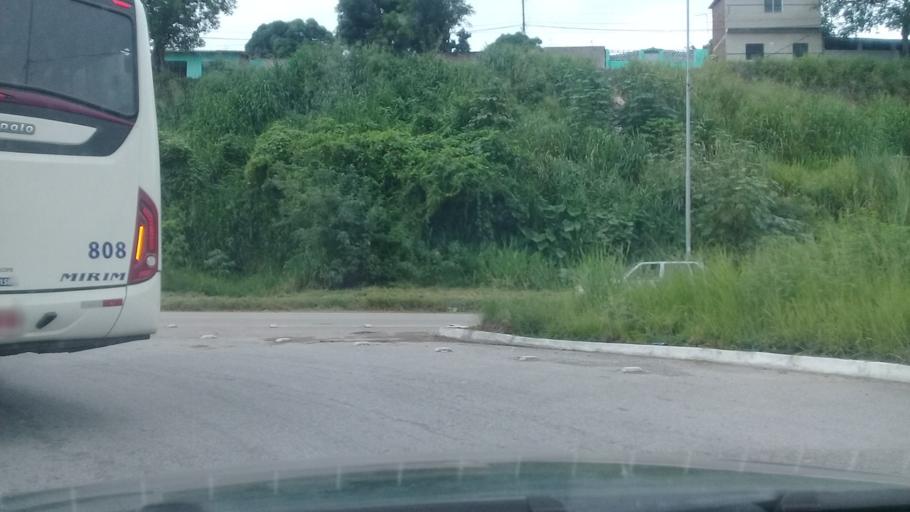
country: BR
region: Pernambuco
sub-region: Jaboatao Dos Guararapes
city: Jaboatao dos Guararapes
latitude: -8.0820
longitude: -34.9918
